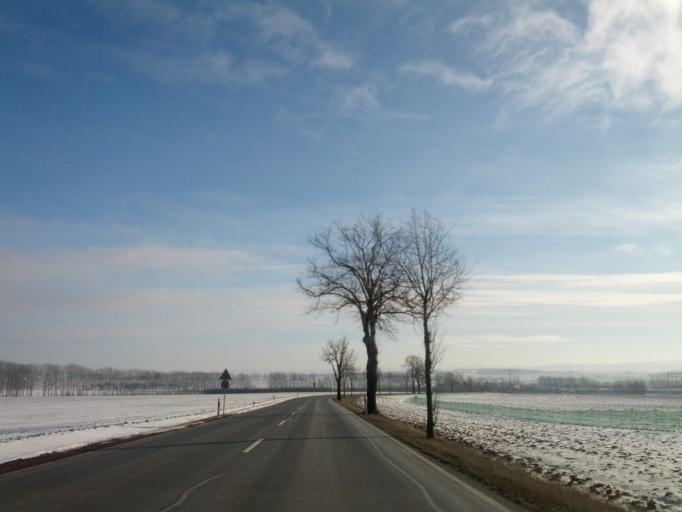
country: DE
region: Thuringia
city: Friedrichswerth
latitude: 51.0350
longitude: 10.5309
